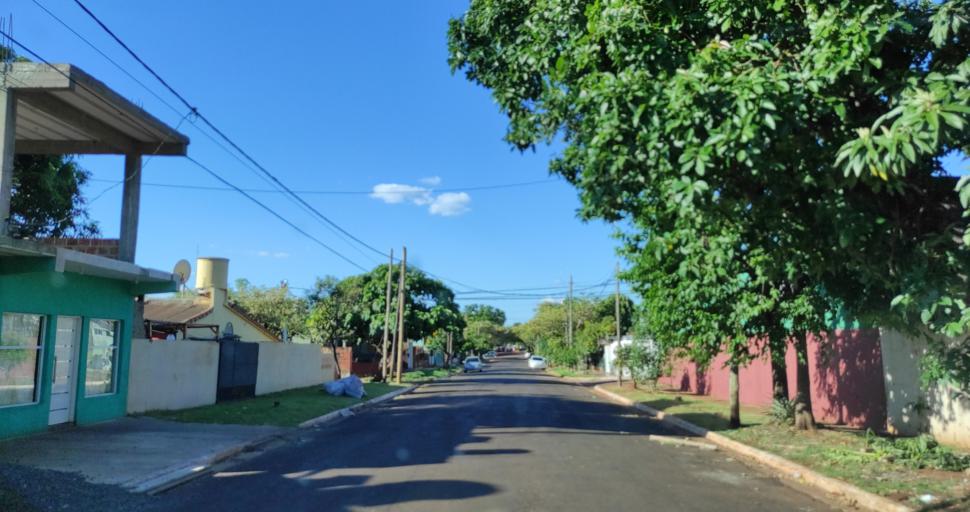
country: AR
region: Misiones
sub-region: Departamento de Capital
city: Posadas
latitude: -27.3757
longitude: -55.9310
